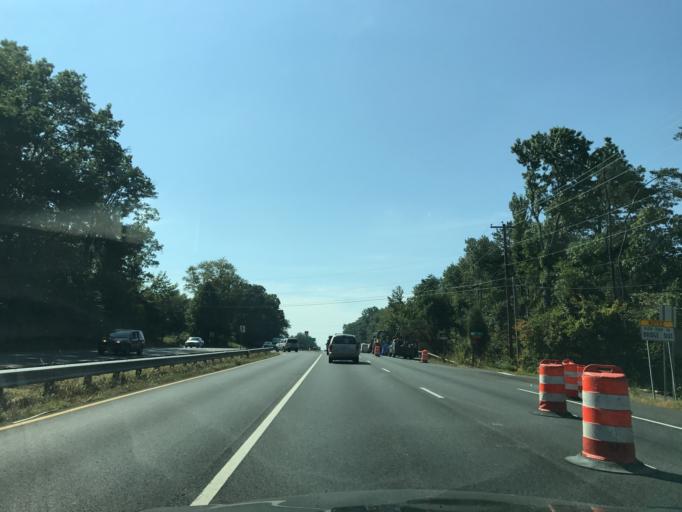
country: US
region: Maryland
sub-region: Cecil County
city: North East
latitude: 39.6043
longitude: -75.9593
